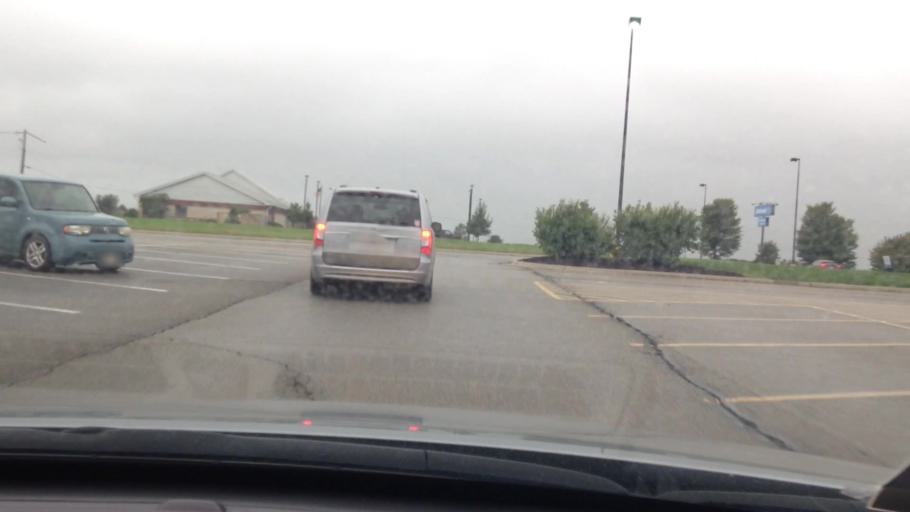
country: US
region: Kansas
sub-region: Brown County
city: Hiawatha
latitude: 39.8464
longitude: -95.5613
